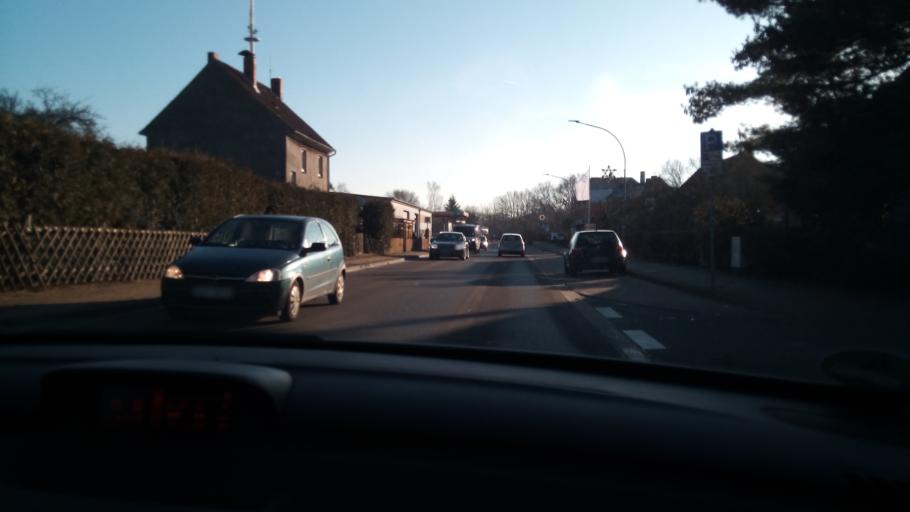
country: DE
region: Schleswig-Holstein
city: Buchen
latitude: 53.4740
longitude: 10.6226
